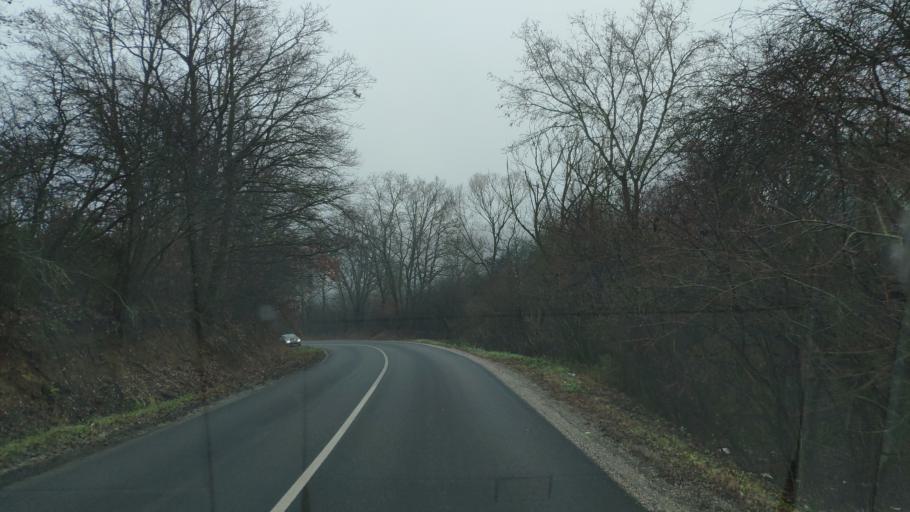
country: SK
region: Kosicky
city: Kosice
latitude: 48.7151
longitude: 21.3067
